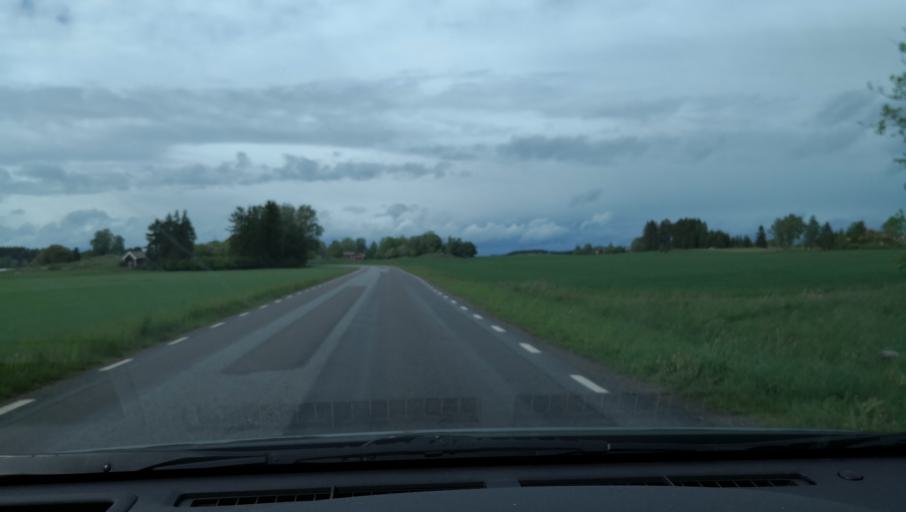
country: SE
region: Uppsala
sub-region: Enkopings Kommun
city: Orsundsbro
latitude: 59.6972
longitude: 17.3685
